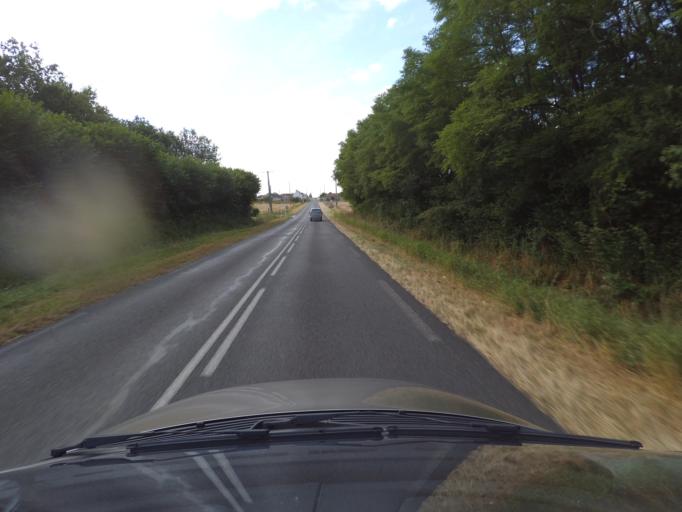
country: FR
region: Centre
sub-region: Departement d'Indre-et-Loire
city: Richelieu
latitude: 46.9866
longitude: 0.3395
